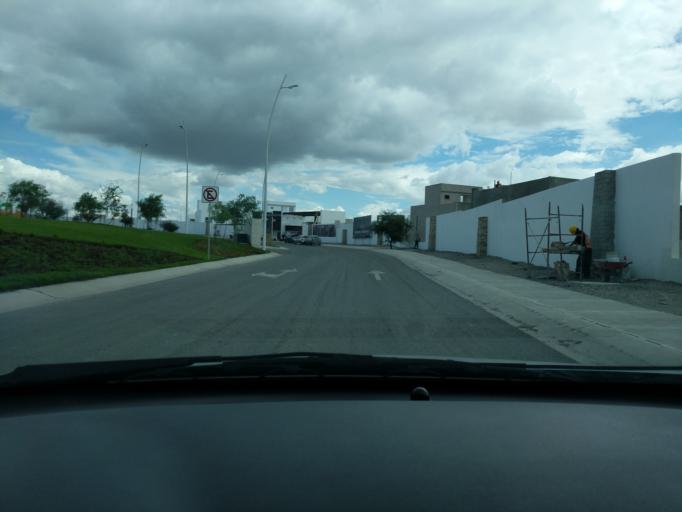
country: MX
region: Queretaro
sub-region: El Marques
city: El Pozo
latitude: 20.6458
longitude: -100.3153
